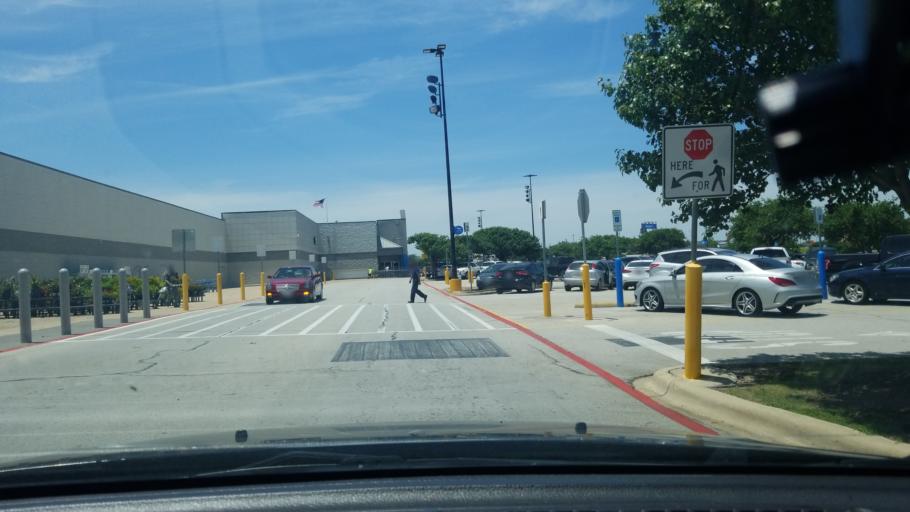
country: US
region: Texas
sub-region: Dallas County
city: Mesquite
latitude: 32.7883
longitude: -96.5978
